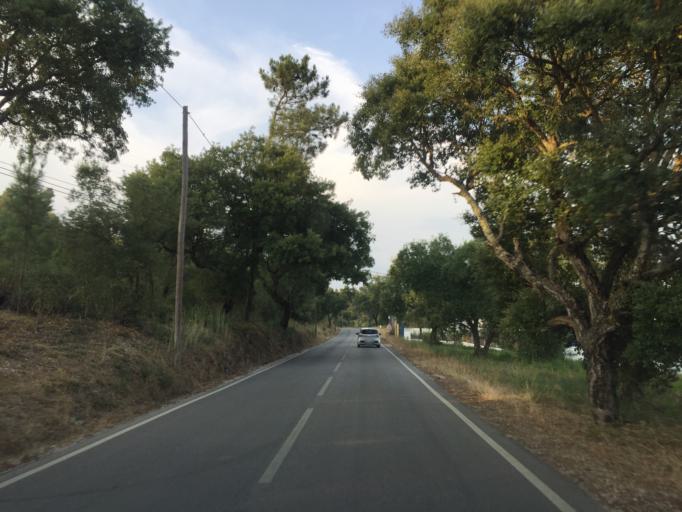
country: PT
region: Santarem
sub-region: Tomar
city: Tomar
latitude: 39.5990
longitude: -8.3154
